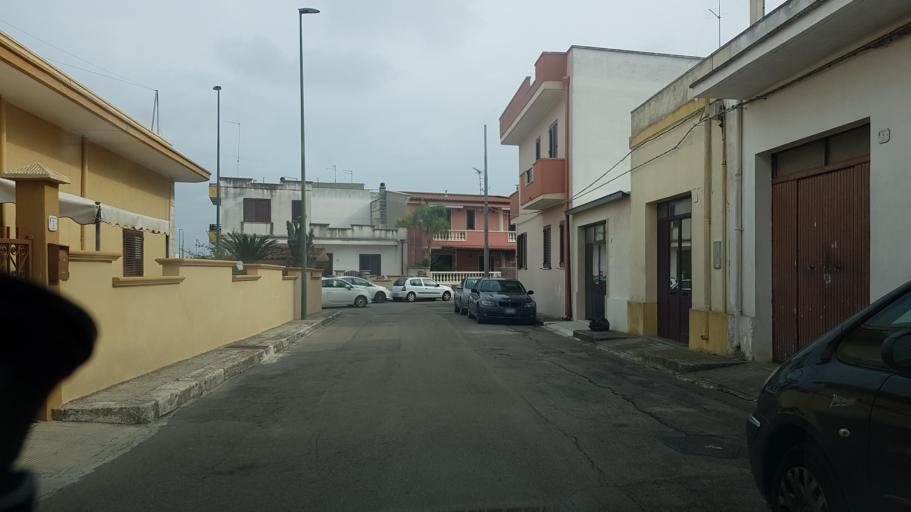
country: IT
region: Apulia
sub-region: Provincia di Lecce
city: Guagnano
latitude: 40.4044
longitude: 17.9468
